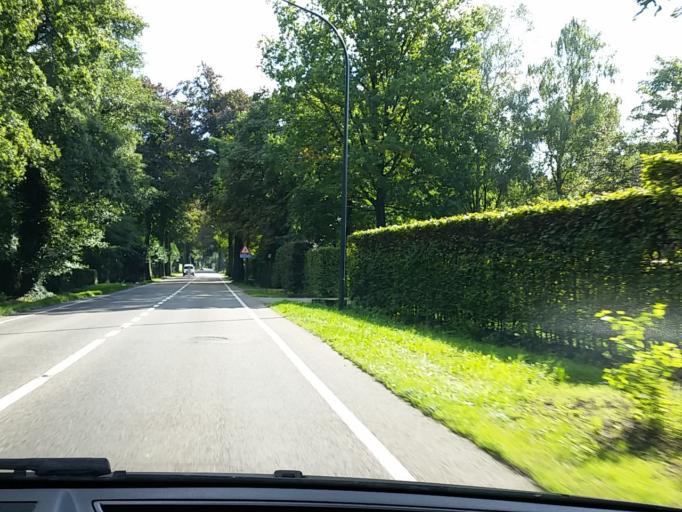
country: BE
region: Flanders
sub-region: Provincie Antwerpen
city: Schilde
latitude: 51.2524
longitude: 4.5635
